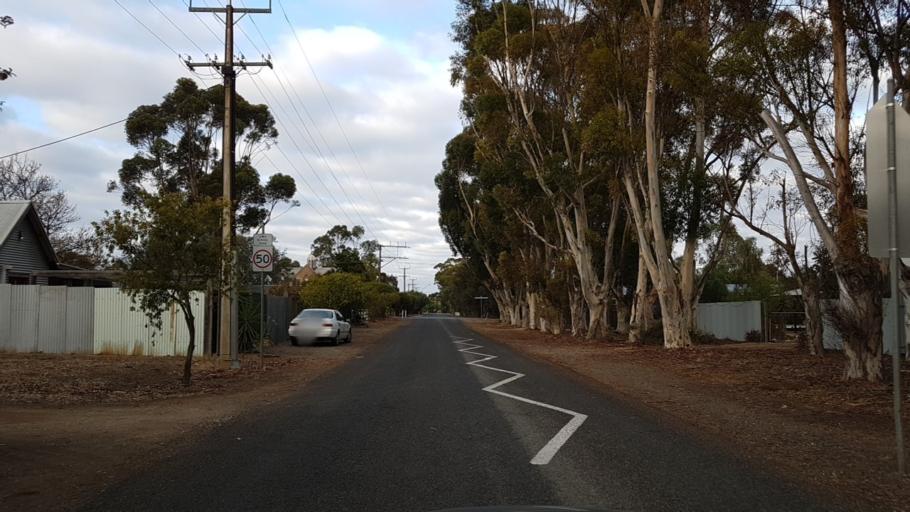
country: AU
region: South Australia
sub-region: Mount Barker
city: Callington
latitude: -35.1151
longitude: 139.0386
